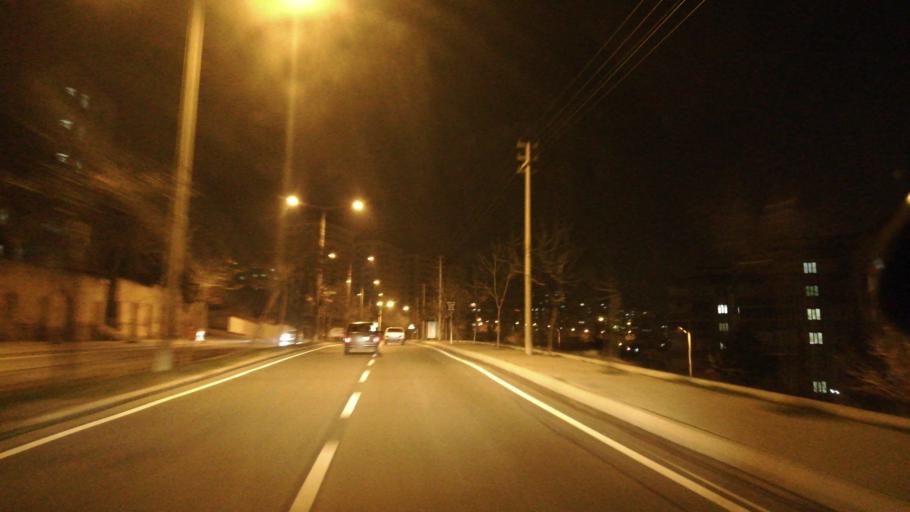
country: TR
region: Kahramanmaras
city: Kahramanmaras
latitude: 37.5976
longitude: 36.8674
